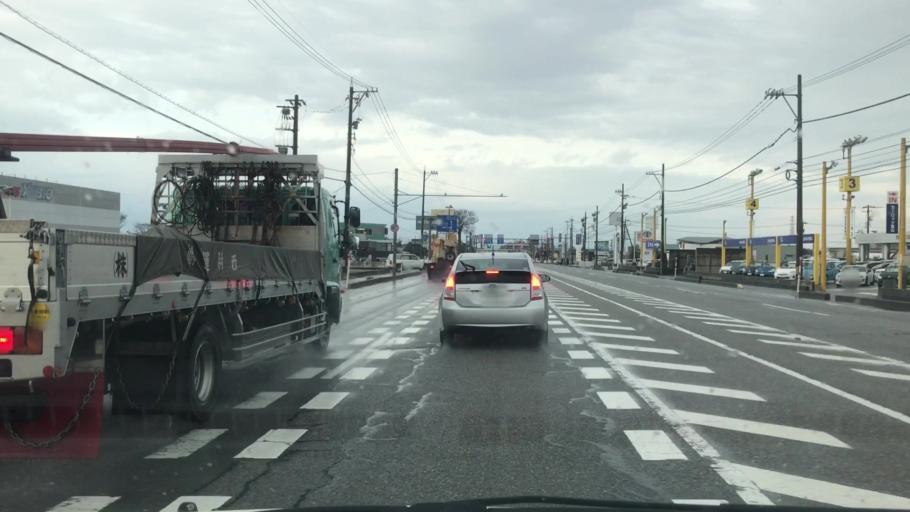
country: JP
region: Toyama
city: Toyama-shi
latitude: 36.6406
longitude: 137.2094
